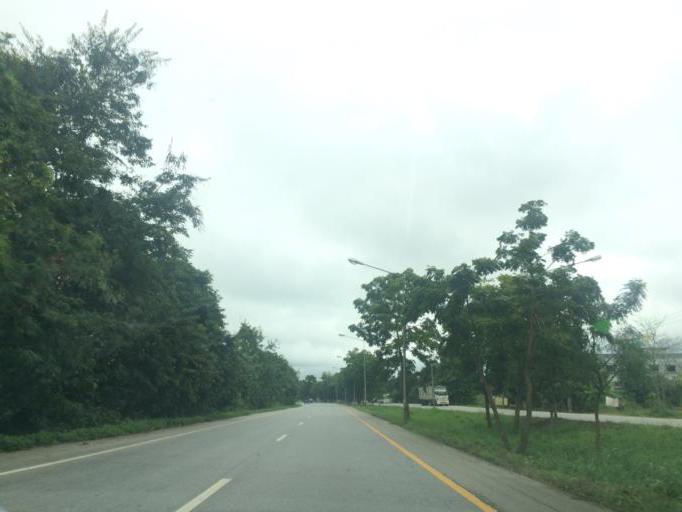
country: TH
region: Chiang Rai
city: Mae Lao
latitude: 19.7948
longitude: 99.7497
